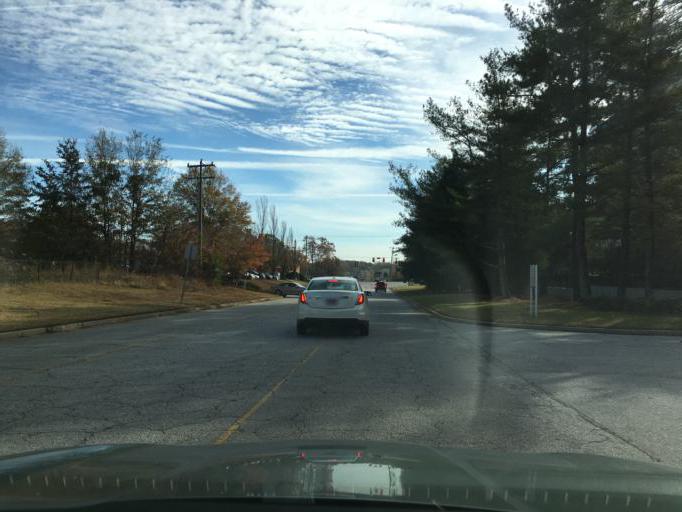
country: US
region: South Carolina
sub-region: Greenville County
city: Wade Hampton
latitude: 34.8436
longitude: -82.3306
